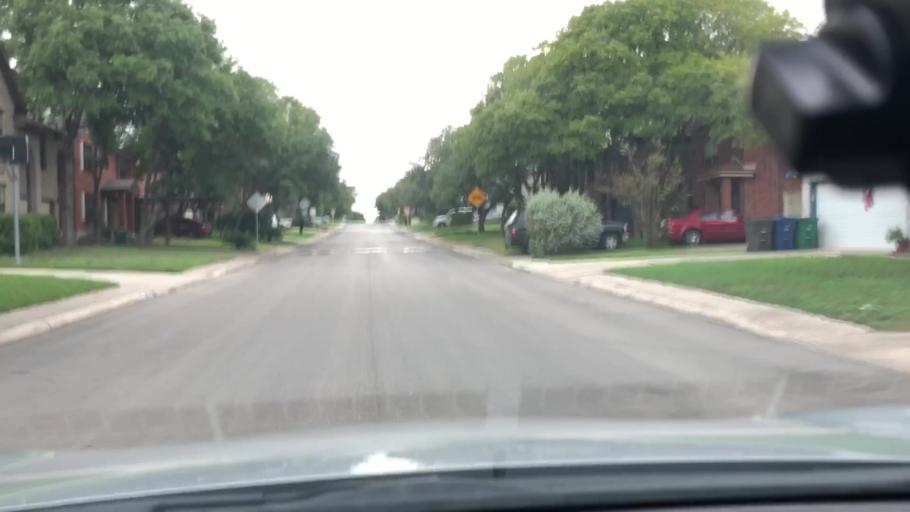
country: US
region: Texas
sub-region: Bexar County
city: Leon Valley
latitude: 29.5000
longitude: -98.6676
